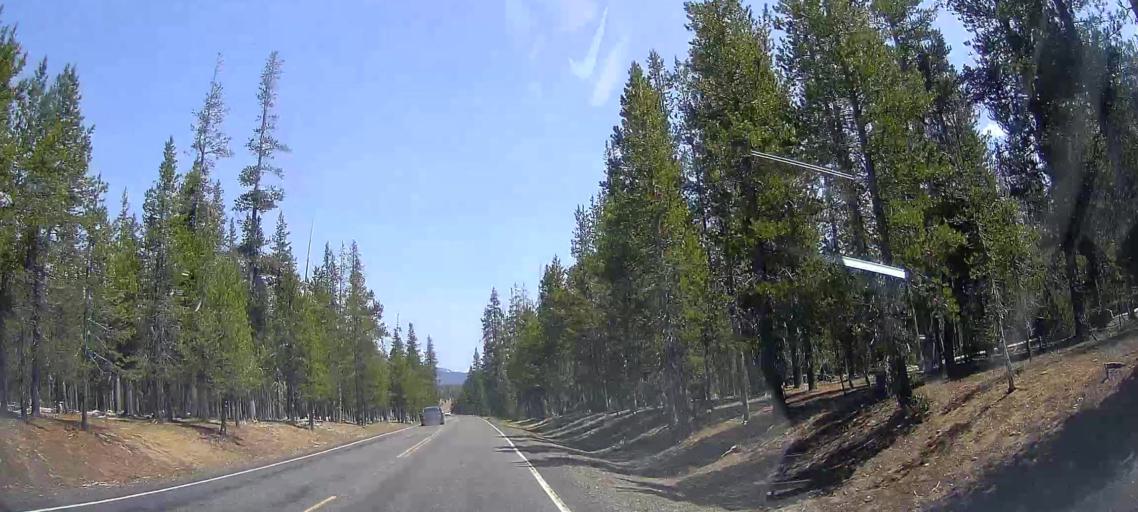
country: US
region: Oregon
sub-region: Lane County
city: Oakridge
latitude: 43.0239
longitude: -122.1212
